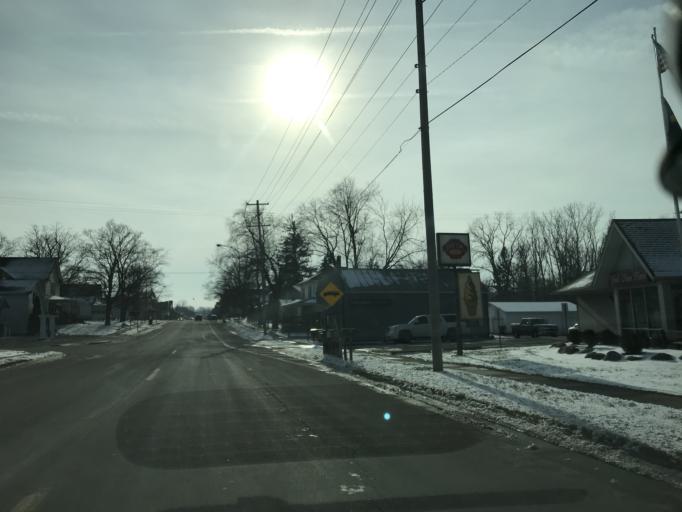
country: US
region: Michigan
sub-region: Barry County
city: Nashville
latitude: 42.6074
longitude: -85.0935
